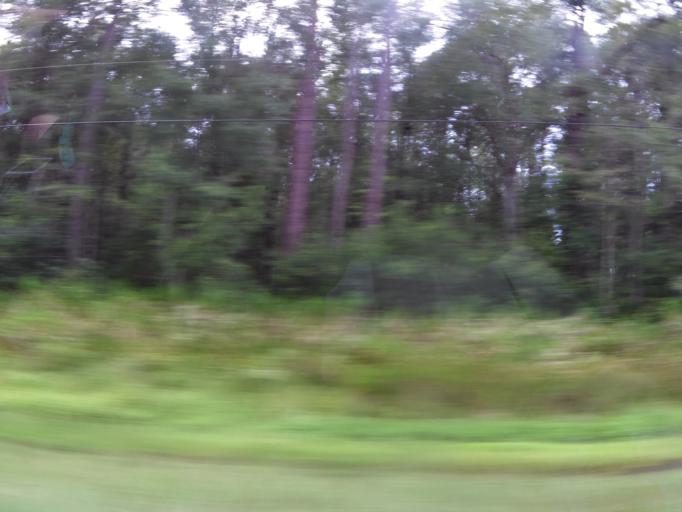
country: US
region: Florida
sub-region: Duval County
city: Baldwin
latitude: 30.3582
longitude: -81.9159
